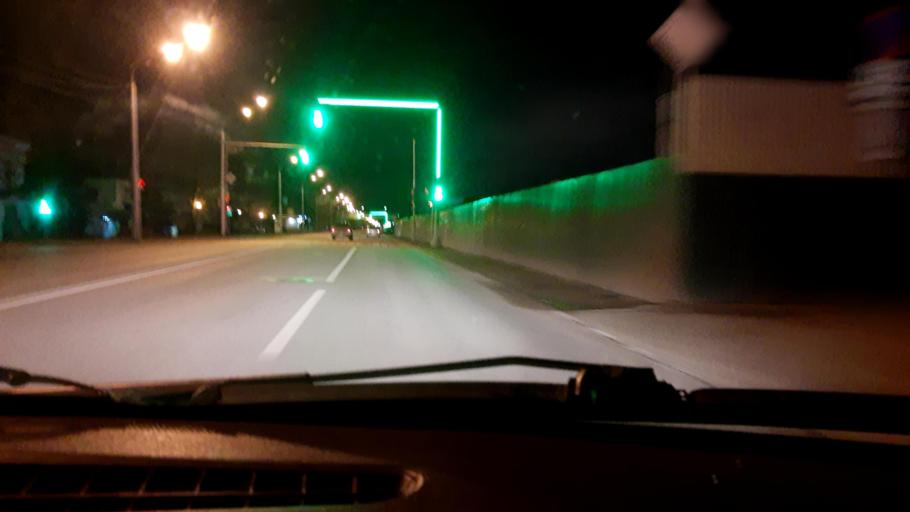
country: RU
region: Bashkortostan
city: Avdon
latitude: 54.6966
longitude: 55.8303
